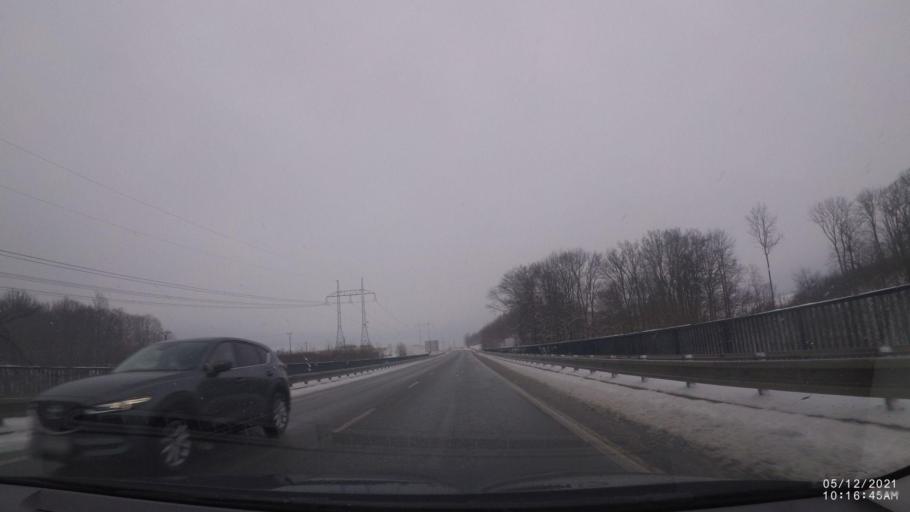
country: CZ
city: Vamberk
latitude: 50.1102
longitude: 16.2805
